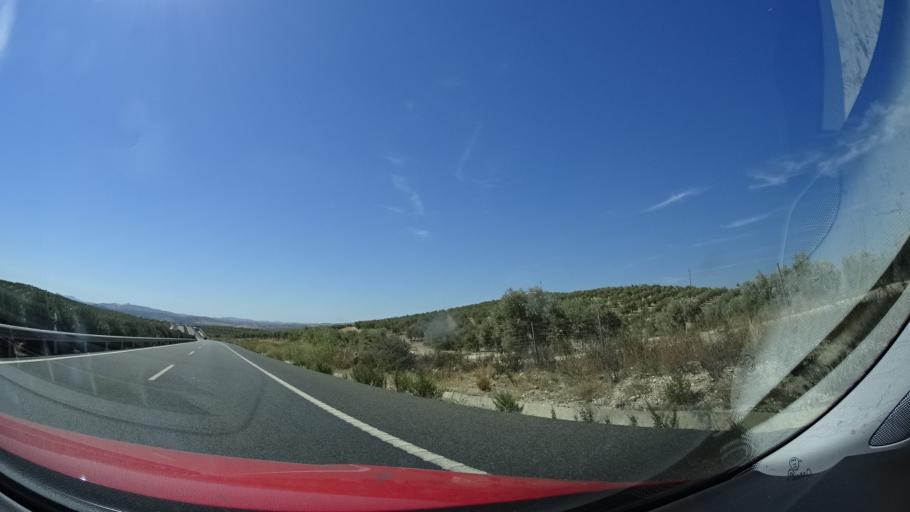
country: ES
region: Andalusia
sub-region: Provincia de Sevilla
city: Gilena
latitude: 37.2735
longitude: -4.9444
